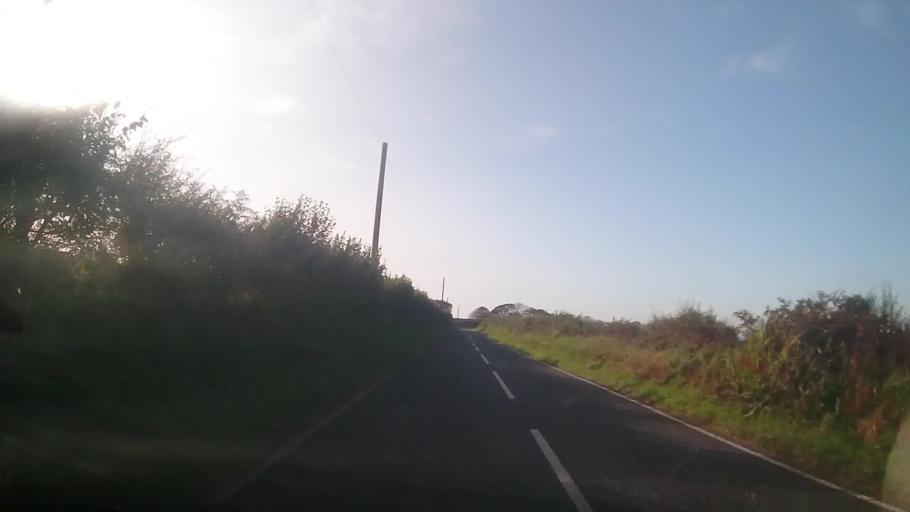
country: GB
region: Wales
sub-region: Pembrokeshire
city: Fishguard
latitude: 51.9704
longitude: -4.9078
